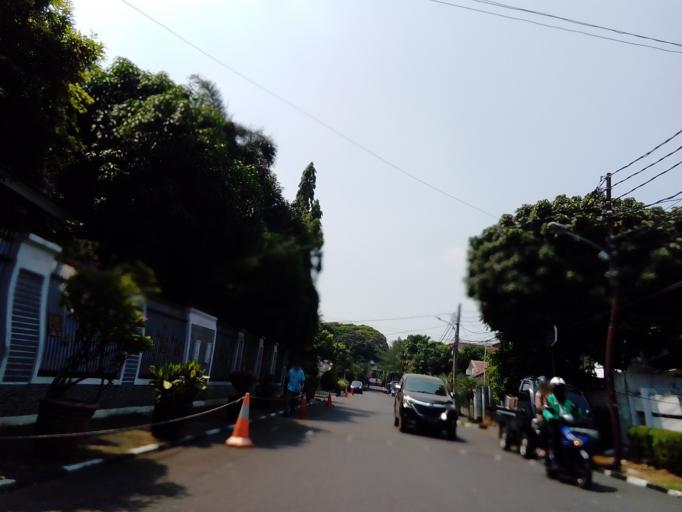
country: ID
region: Jakarta Raya
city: Jakarta
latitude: -6.2624
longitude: 106.7989
